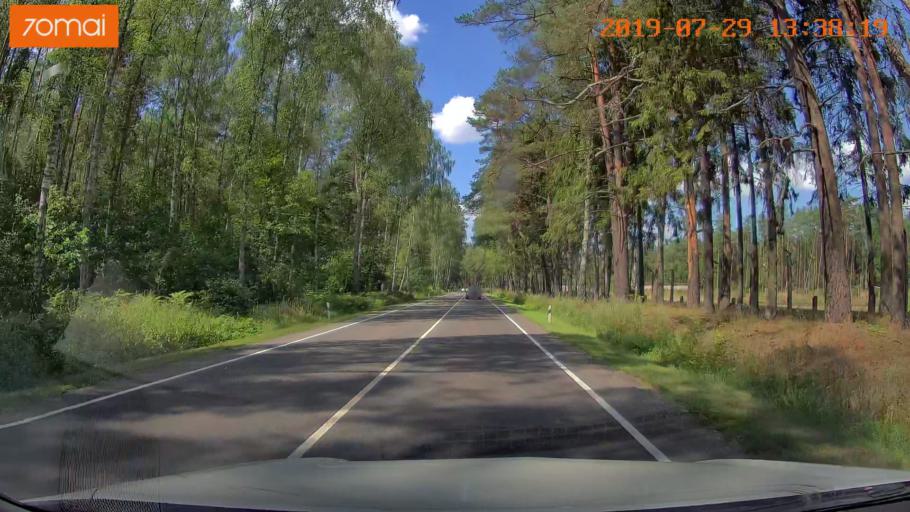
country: RU
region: Kaliningrad
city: Volochayevskoye
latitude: 54.7204
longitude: 20.1726
